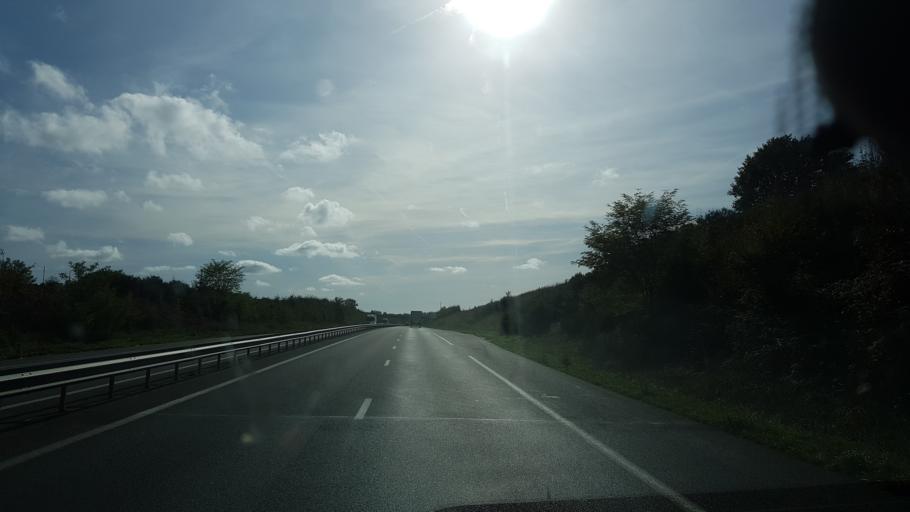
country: FR
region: Poitou-Charentes
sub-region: Departement de la Charente
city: Taponnat-Fleurignac
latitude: 45.7676
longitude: 0.3985
